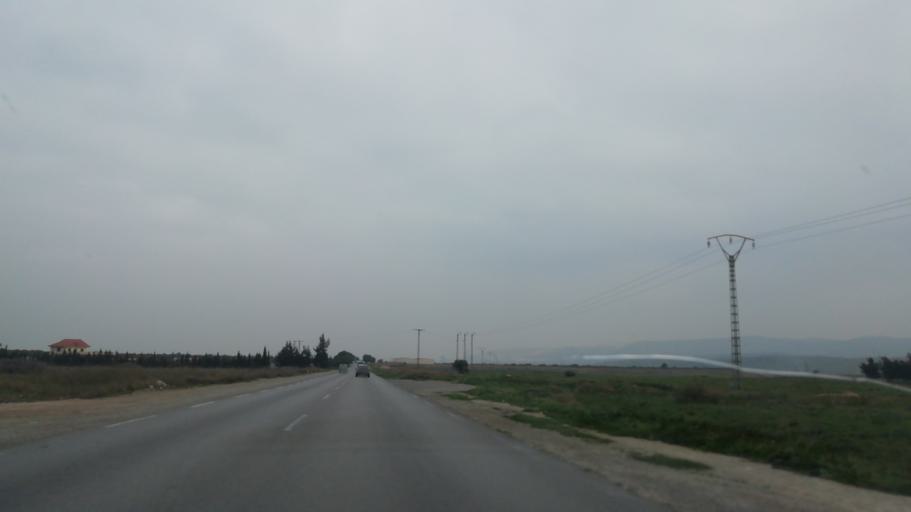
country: DZ
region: Mascara
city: Sig
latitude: 35.5385
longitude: -0.3562
